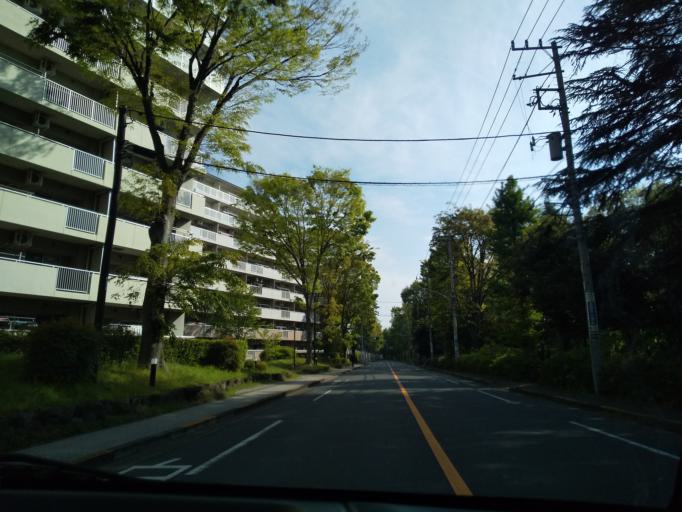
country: JP
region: Tokyo
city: Hino
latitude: 35.6633
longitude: 139.3832
